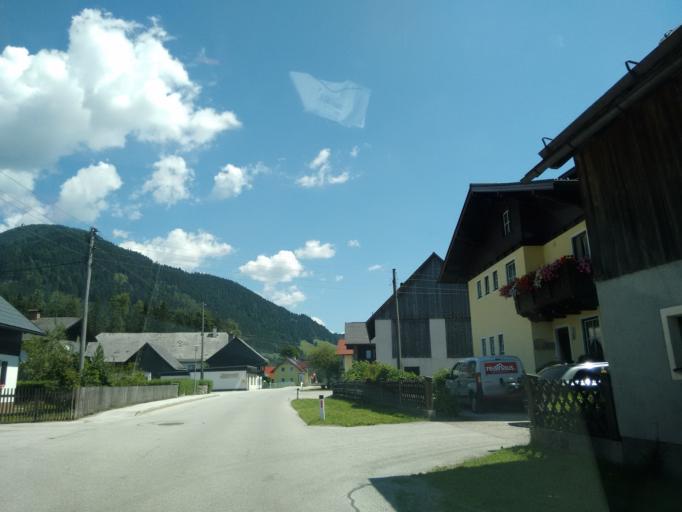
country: AT
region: Styria
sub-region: Politischer Bezirk Liezen
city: Tauplitz
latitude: 47.5541
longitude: 13.9567
